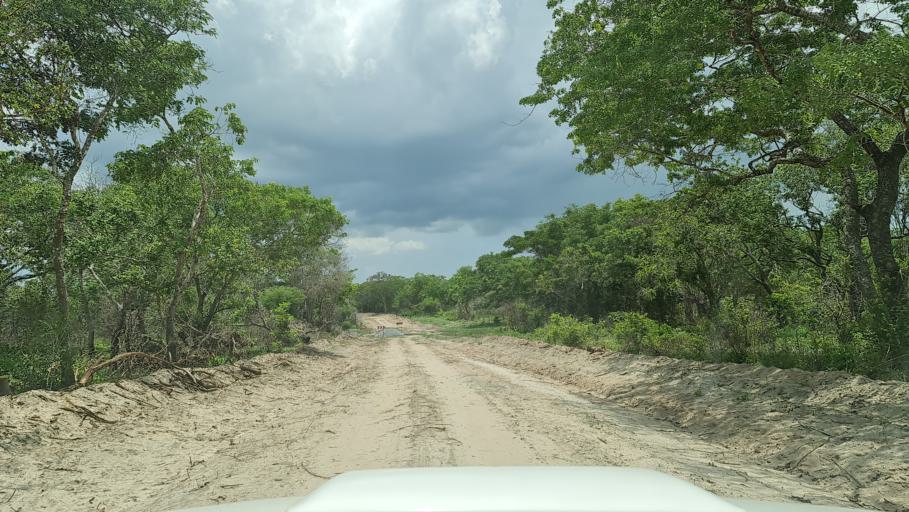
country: MZ
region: Nampula
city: Ilha de Mocambique
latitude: -15.2438
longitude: 40.3645
